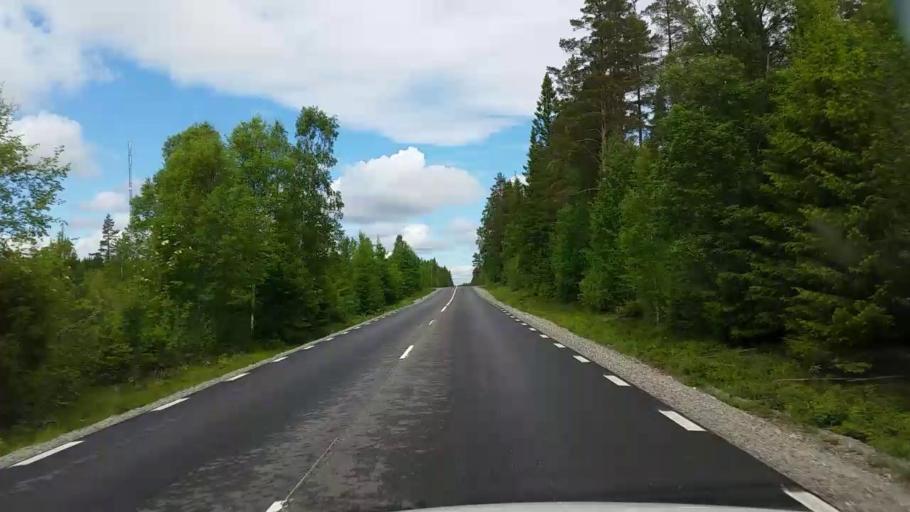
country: SE
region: Gaevleborg
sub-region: Sandvikens Kommun
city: Jarbo
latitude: 60.9097
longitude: 16.3756
